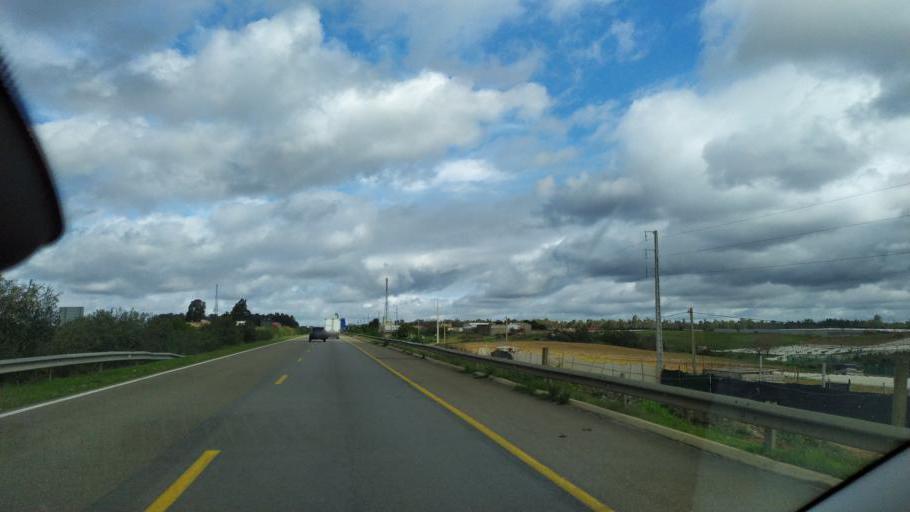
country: MA
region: Gharb-Chrarda-Beni Hssen
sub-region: Kenitra Province
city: Lalla Mimouna
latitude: 34.8683
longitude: -6.2180
